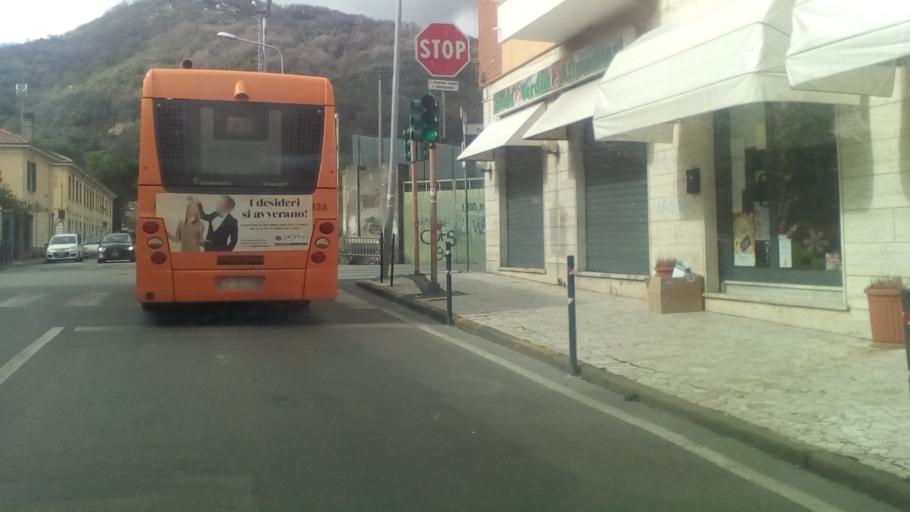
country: IT
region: Tuscany
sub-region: Provincia di Massa-Carrara
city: Carrara
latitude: 44.0640
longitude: 10.0774
